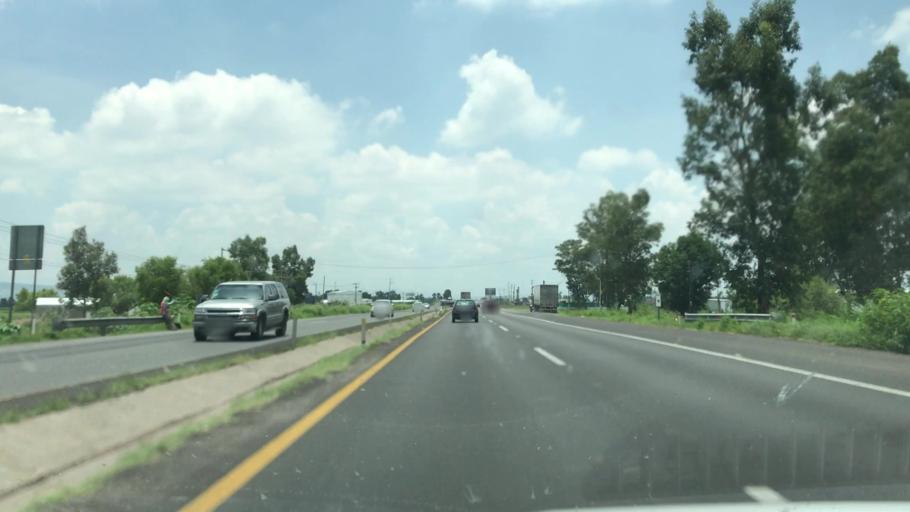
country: MX
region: Guanajuato
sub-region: Irapuato
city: San Jose de Bernalejo (El Guayabo)
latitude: 20.6088
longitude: -101.4100
